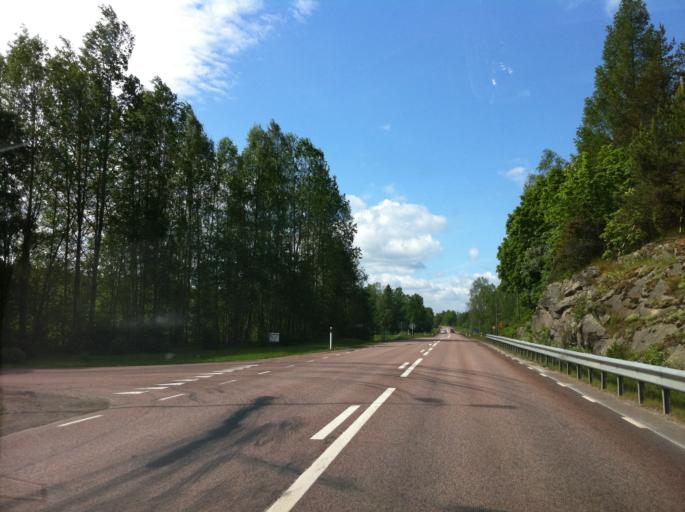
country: SE
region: Vaermland
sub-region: Karlstads Kommun
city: Valberg
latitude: 59.3797
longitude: 13.1641
